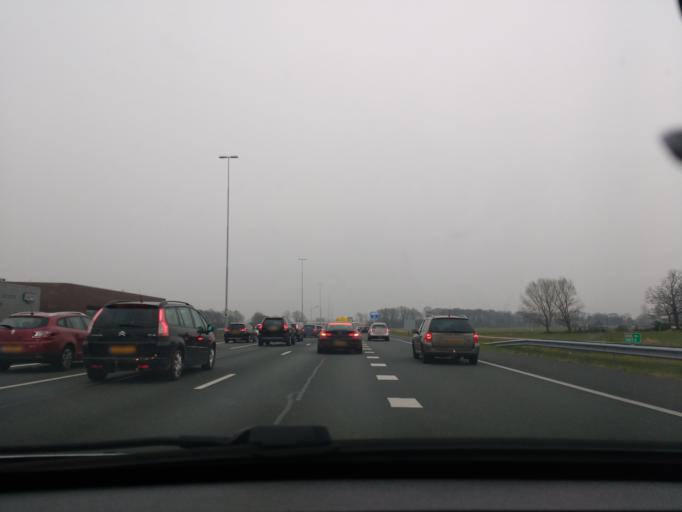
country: NL
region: Gelderland
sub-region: Gemeente Ede
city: Ede
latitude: 52.0208
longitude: 5.6247
